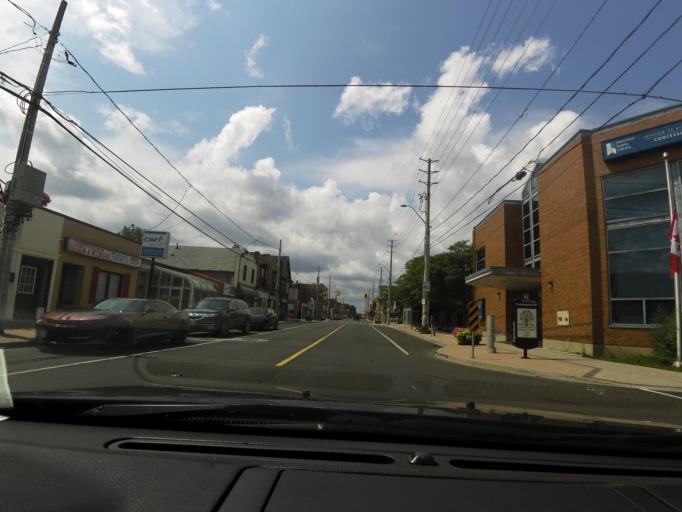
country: CA
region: Ontario
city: Hamilton
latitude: 43.2408
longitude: -79.8512
